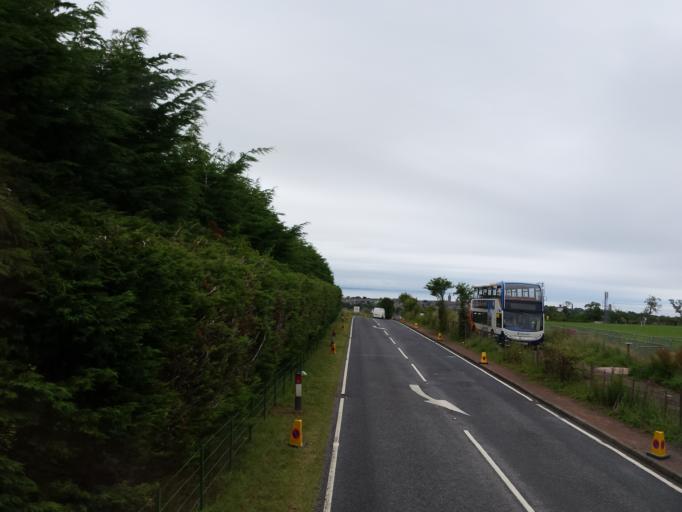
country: GB
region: Scotland
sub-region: Fife
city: Saint Andrews
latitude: 56.3242
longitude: -2.8124
